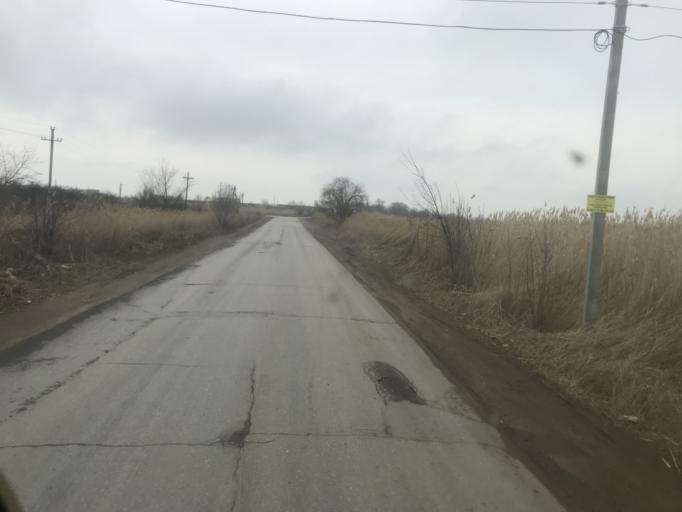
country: RU
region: Volgograd
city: Svetlyy Yar
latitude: 48.5282
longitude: 44.6113
